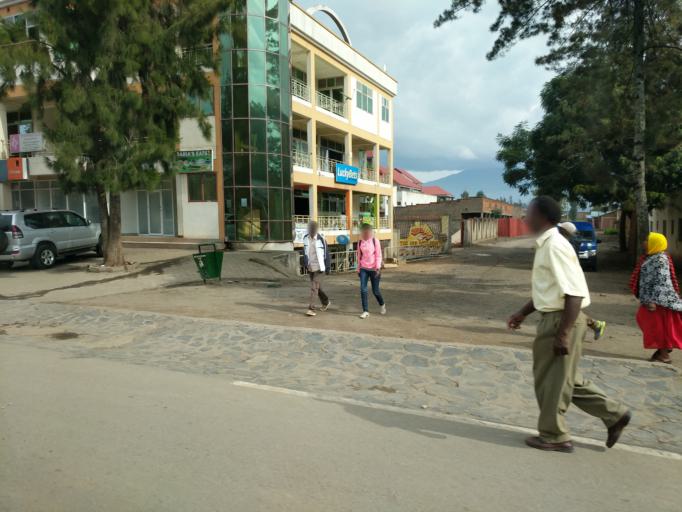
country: RW
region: Northern Province
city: Musanze
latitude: -1.5092
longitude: 29.6448
